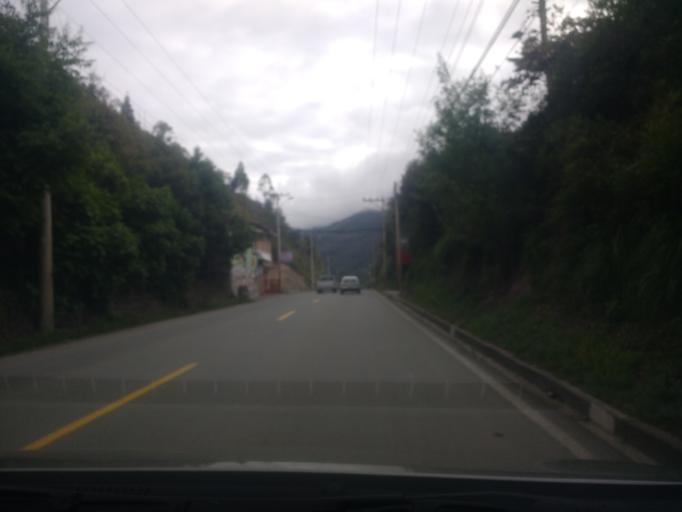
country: EC
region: Azuay
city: La Union
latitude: -2.8481
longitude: -78.7759
